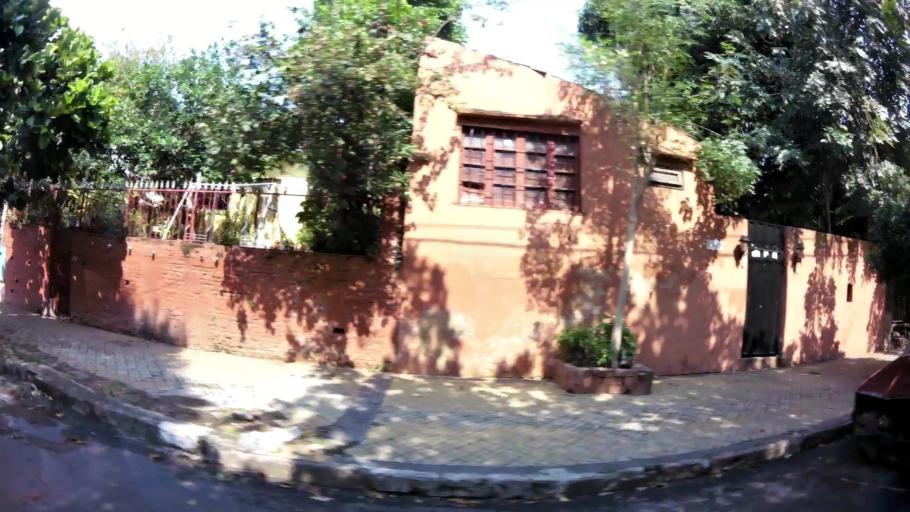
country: PY
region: Presidente Hayes
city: Nanawa
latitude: -25.2853
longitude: -57.6599
